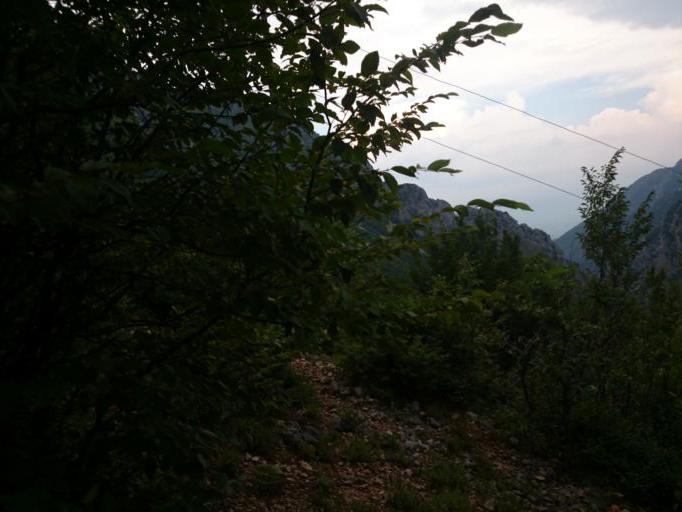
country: AL
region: Diber
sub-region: Rrethi i Dibres
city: Fushe-Lure
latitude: 41.7625
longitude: 20.2258
